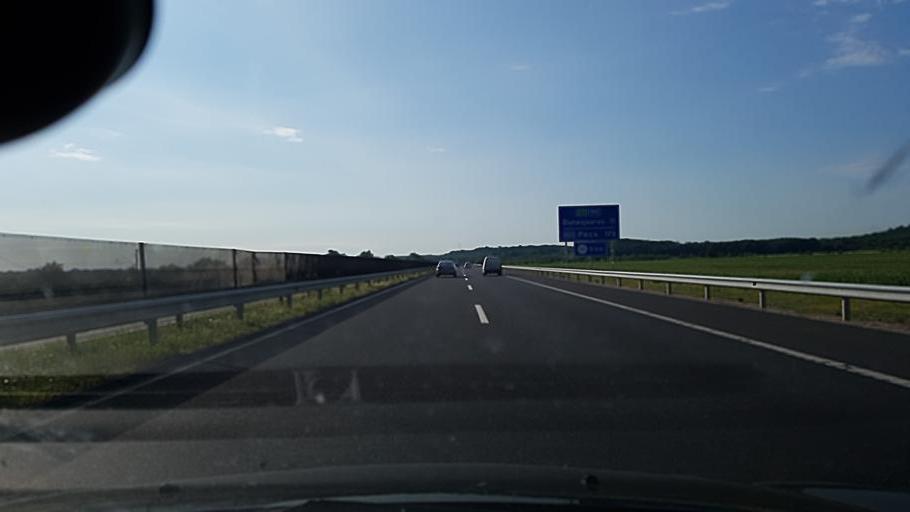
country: HU
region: Fejer
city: Adony
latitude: 47.0862
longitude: 18.8641
